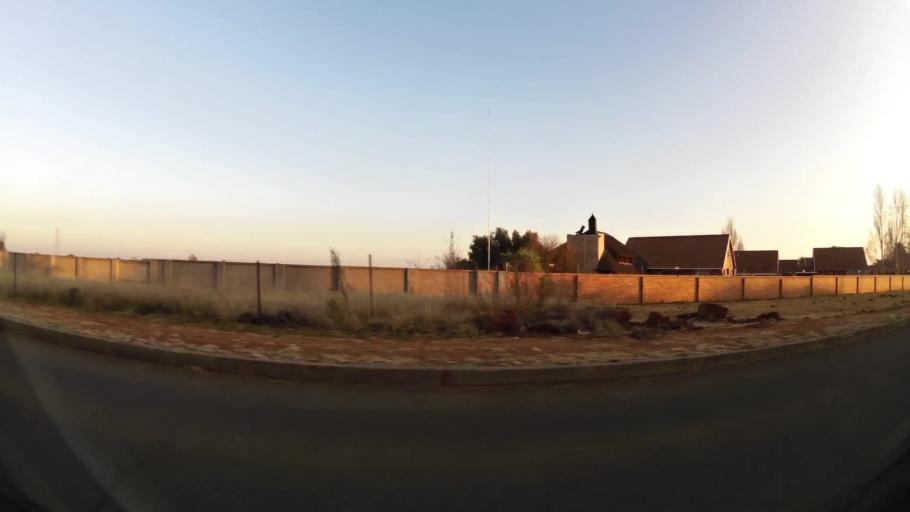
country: ZA
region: Orange Free State
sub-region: Mangaung Metropolitan Municipality
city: Bloemfontein
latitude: -29.0930
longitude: 26.1496
